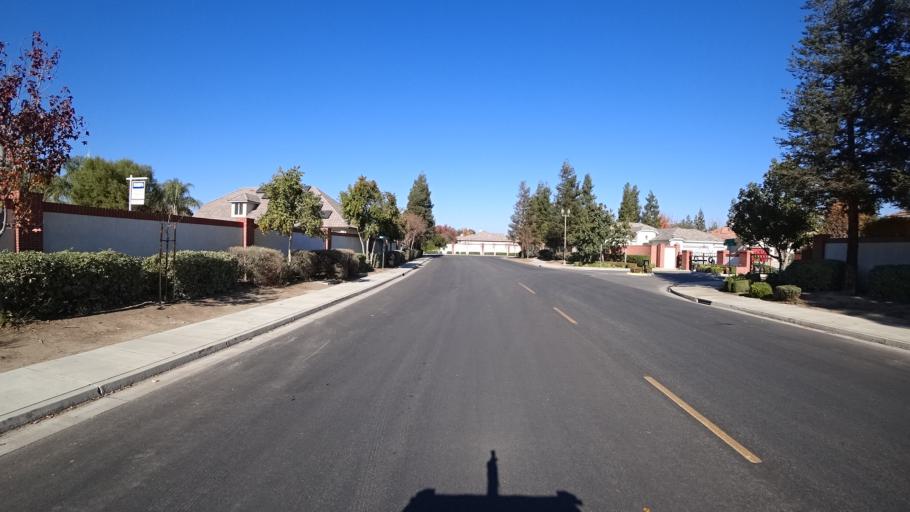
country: US
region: California
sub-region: Kern County
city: Greenacres
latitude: 35.3314
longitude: -119.1157
